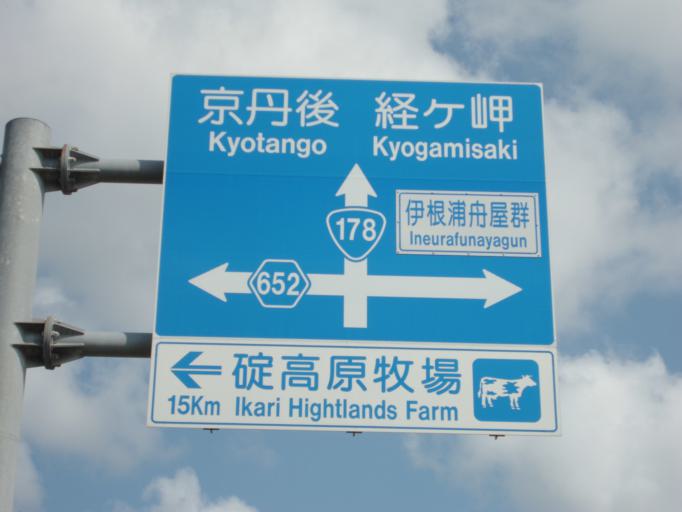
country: JP
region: Kyoto
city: Miyazu
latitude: 35.6736
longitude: 135.2723
